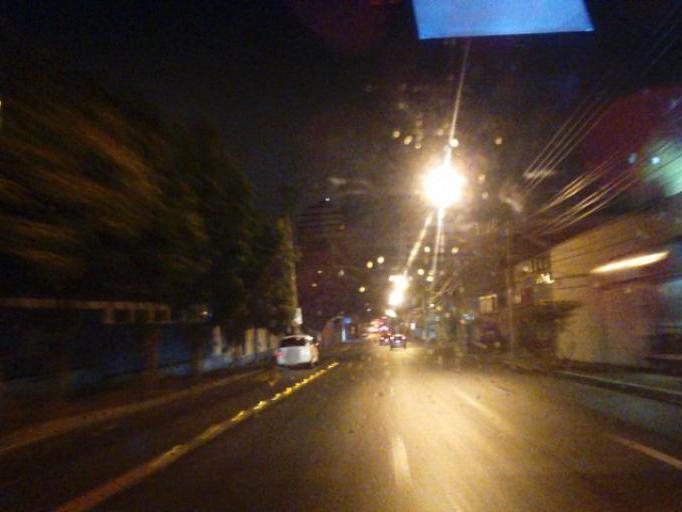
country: BR
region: Sao Paulo
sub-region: Sao Jose Dos Campos
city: Sao Jose dos Campos
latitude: -23.2037
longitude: -45.8958
